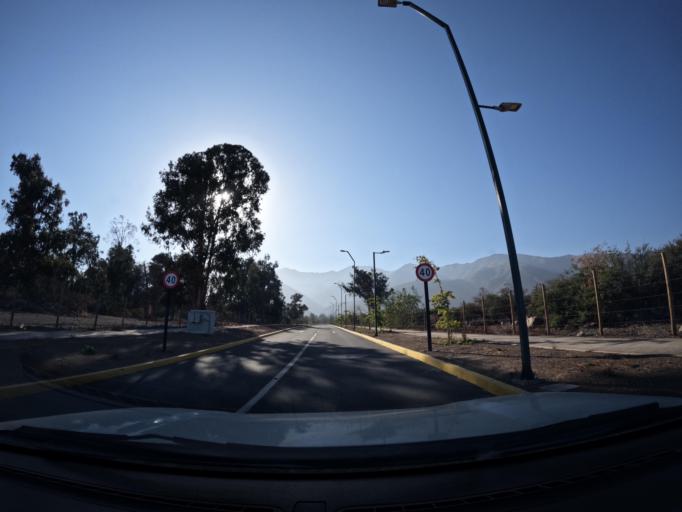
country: CL
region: Santiago Metropolitan
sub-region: Provincia de Santiago
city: Villa Presidente Frei, Nunoa, Santiago, Chile
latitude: -33.5021
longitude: -70.5398
